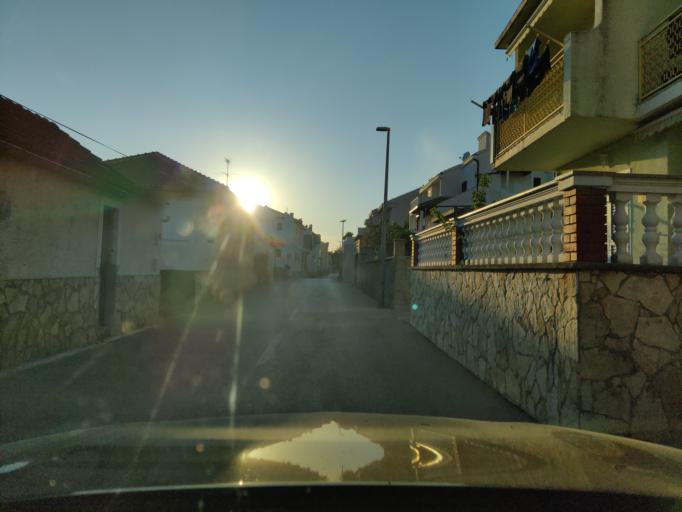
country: HR
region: Sibensko-Kniniska
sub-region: Grad Sibenik
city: Tisno
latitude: 43.8018
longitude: 15.6378
